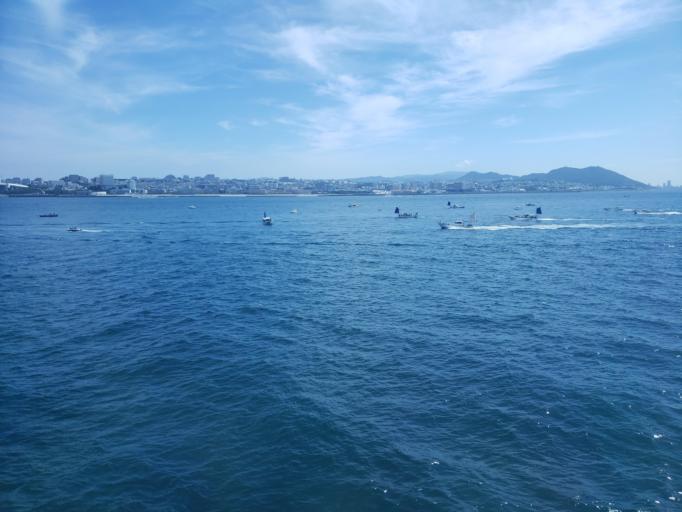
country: JP
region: Hyogo
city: Akashi
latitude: 34.6124
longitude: 135.0338
